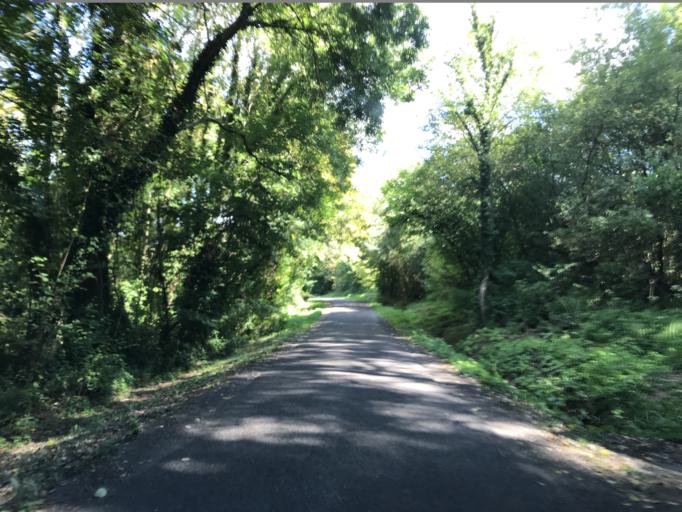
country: FR
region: Haute-Normandie
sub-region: Departement de l'Eure
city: La Chapelle-Reanville
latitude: 49.1086
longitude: 1.3852
